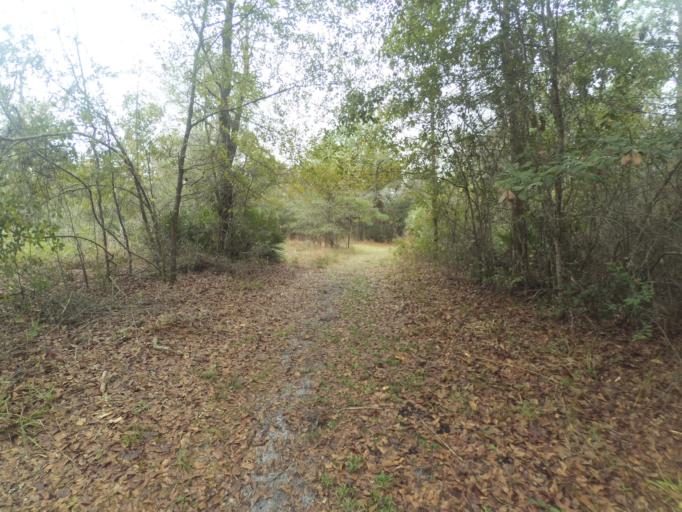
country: US
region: Florida
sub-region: Alachua County
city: Gainesville
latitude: 29.5371
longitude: -82.2806
